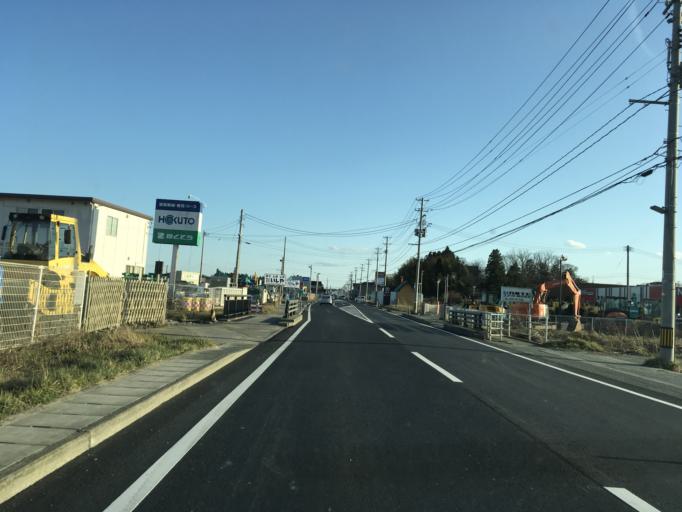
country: JP
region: Iwate
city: Ofunato
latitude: 38.8570
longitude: 141.5802
